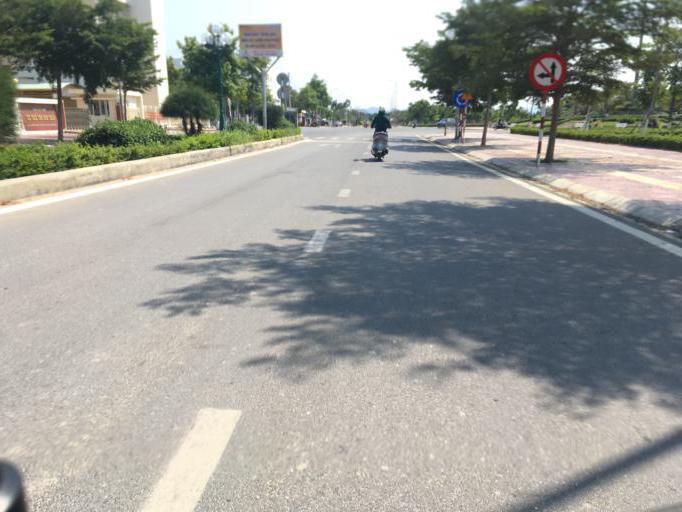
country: VN
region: Ninh Thuan
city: Phan Rang-Thap Cham
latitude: 11.5662
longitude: 109.0010
